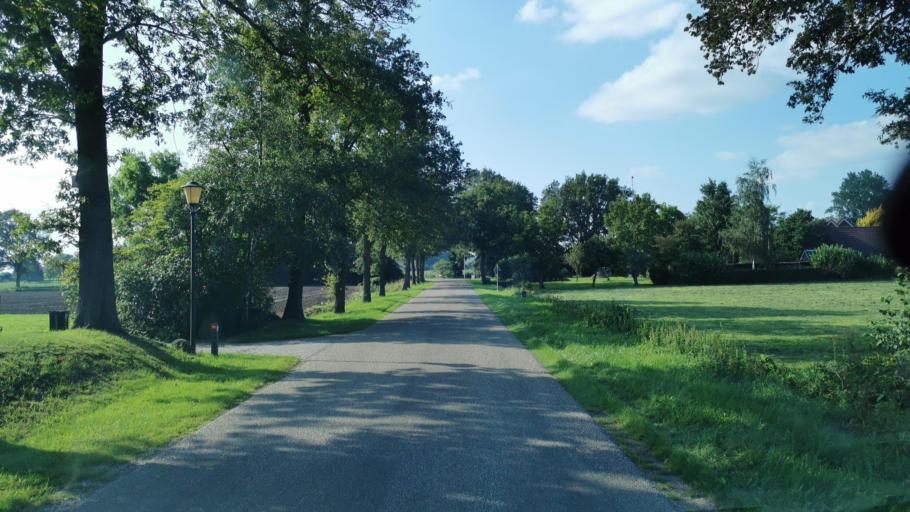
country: NL
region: Overijssel
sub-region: Gemeente Borne
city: Borne
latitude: 52.3426
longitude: 6.7723
